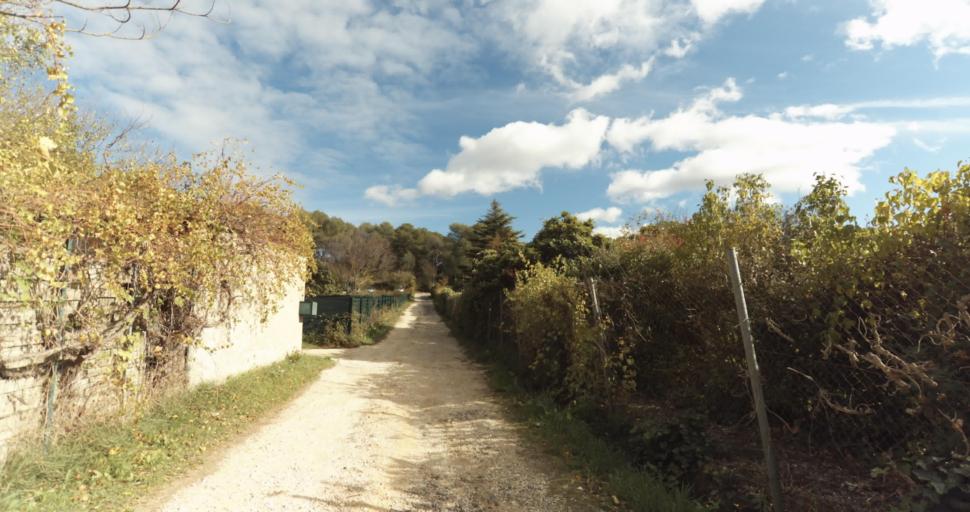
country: FR
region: Provence-Alpes-Cote d'Azur
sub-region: Departement des Bouches-du-Rhone
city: Venelles
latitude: 43.6122
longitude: 5.4905
